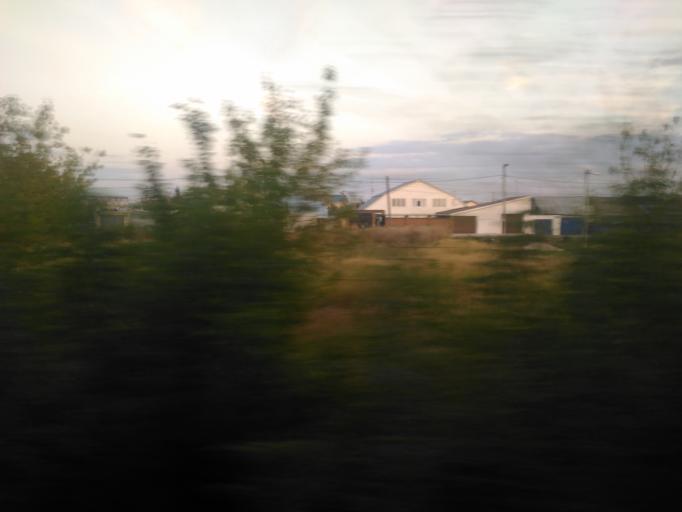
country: RU
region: Ulyanovsk
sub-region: Ulyanovskiy Rayon
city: Ulyanovsk
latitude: 54.2655
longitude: 48.2822
